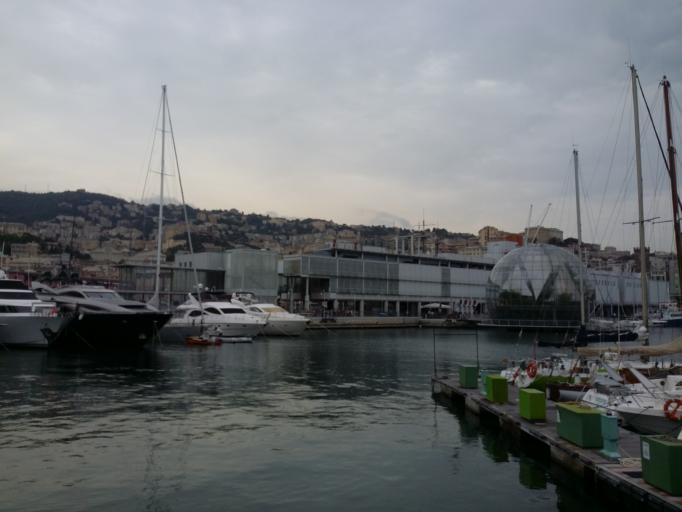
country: IT
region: Liguria
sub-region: Provincia di Genova
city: San Teodoro
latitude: 44.4092
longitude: 8.9240
